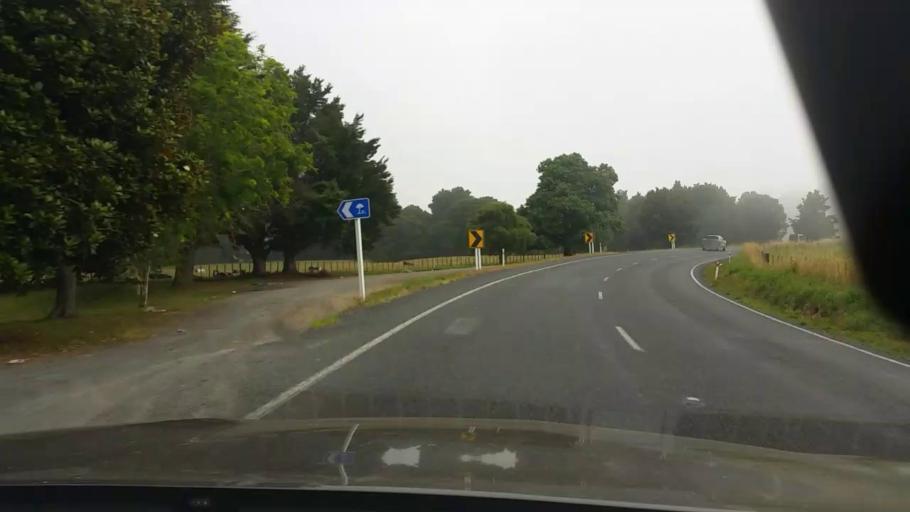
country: NZ
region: Waikato
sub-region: Waikato District
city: Ngaruawahia
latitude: -37.6411
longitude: 175.2946
